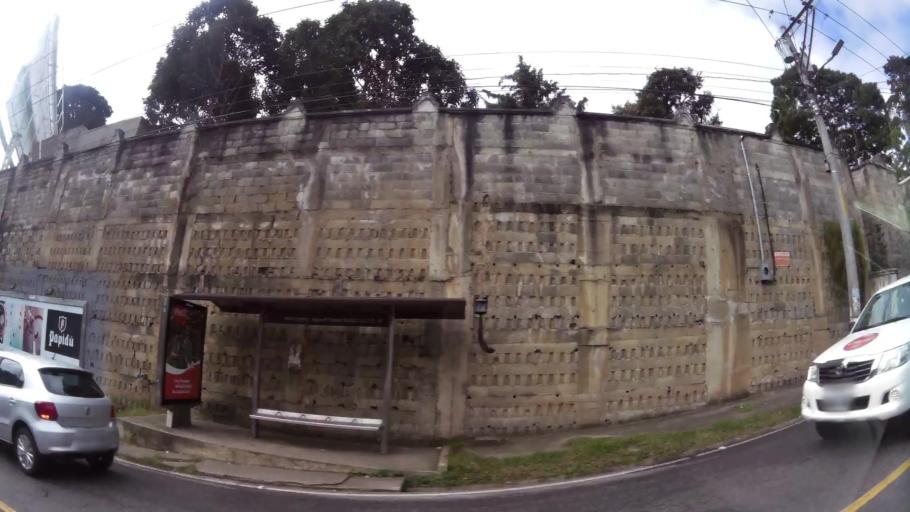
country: GT
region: Guatemala
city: Santa Catarina Pinula
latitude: 14.5622
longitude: -90.4787
